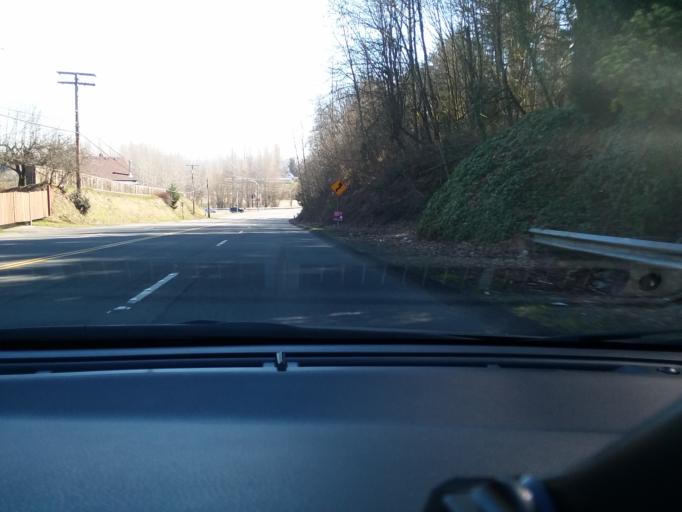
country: US
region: Washington
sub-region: Pierce County
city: Waller
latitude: 47.1915
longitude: -122.3390
